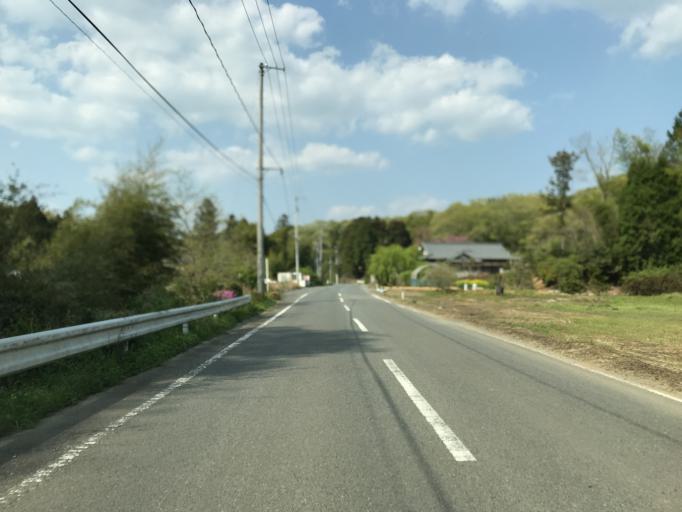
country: JP
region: Fukushima
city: Iwaki
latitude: 36.9801
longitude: 140.7628
